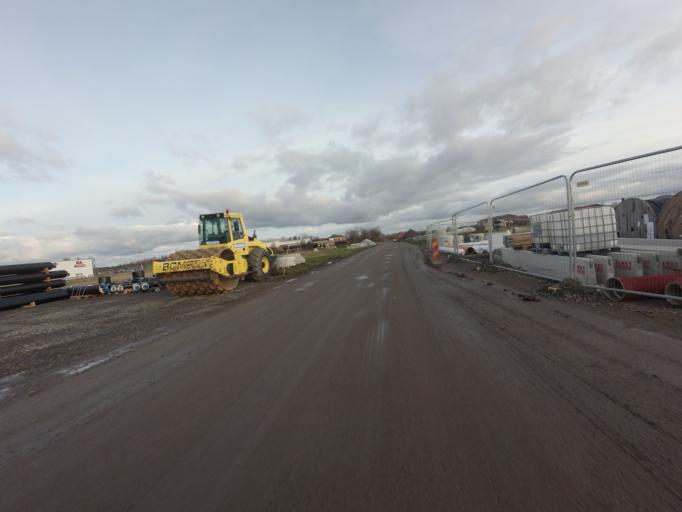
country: SE
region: Skane
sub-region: Hoganas Kommun
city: Hoganas
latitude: 56.1902
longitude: 12.5688
